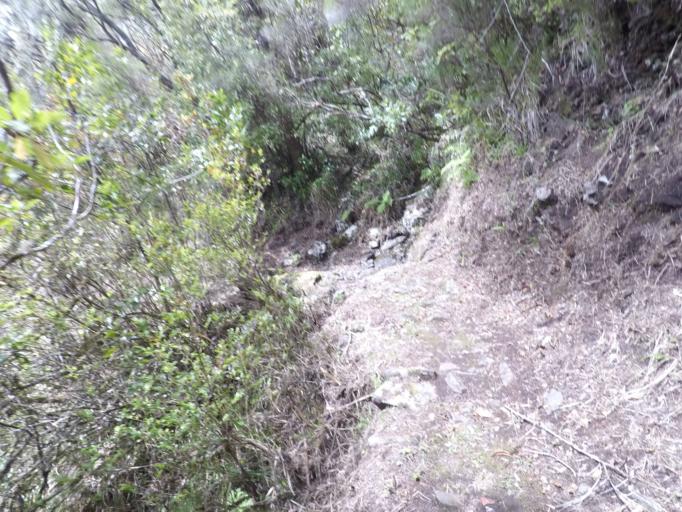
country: PT
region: Madeira
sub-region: Camara de Lobos
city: Curral das Freiras
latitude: 32.7645
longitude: -16.9742
